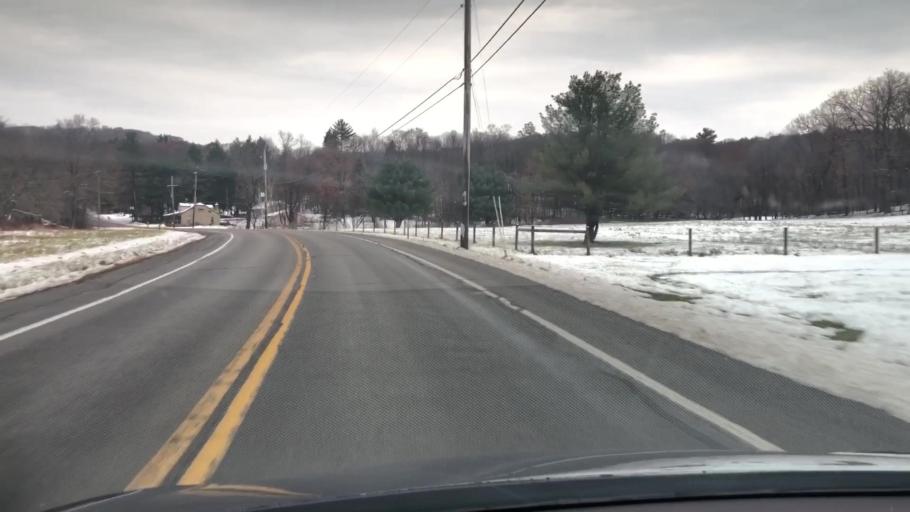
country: US
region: Pennsylvania
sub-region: Jefferson County
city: Brookville
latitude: 41.1370
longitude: -79.1462
